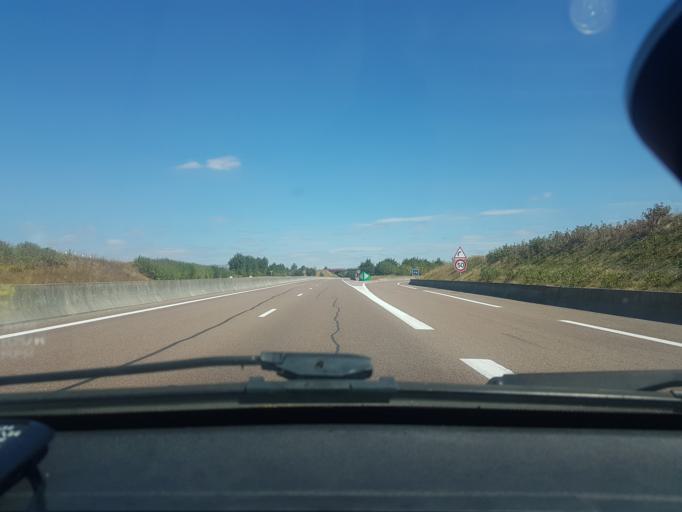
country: FR
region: Bourgogne
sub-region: Departement de la Cote-d'Or
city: Varois-et-Chaignot
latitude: 47.3432
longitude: 5.1370
